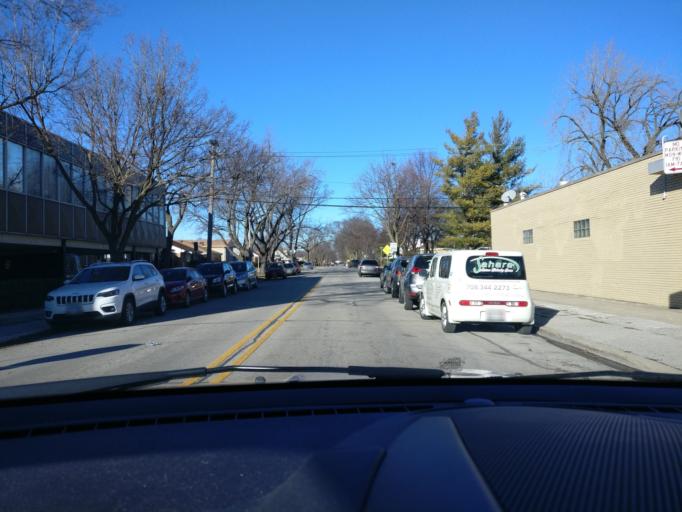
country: US
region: Illinois
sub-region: Cook County
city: Skokie
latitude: 42.0336
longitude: -87.7571
